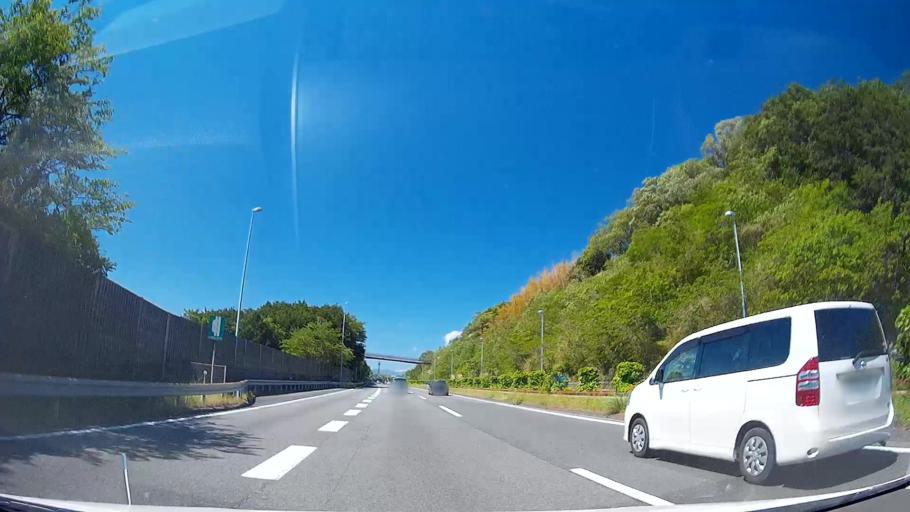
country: JP
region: Shizuoka
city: Mishima
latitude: 35.1935
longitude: 138.9032
